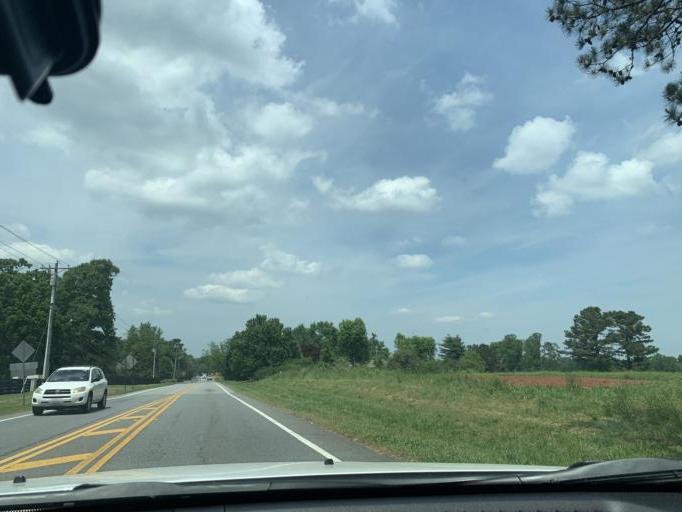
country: US
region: Georgia
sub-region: Forsyth County
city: Cumming
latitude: 34.1423
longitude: -84.1482
